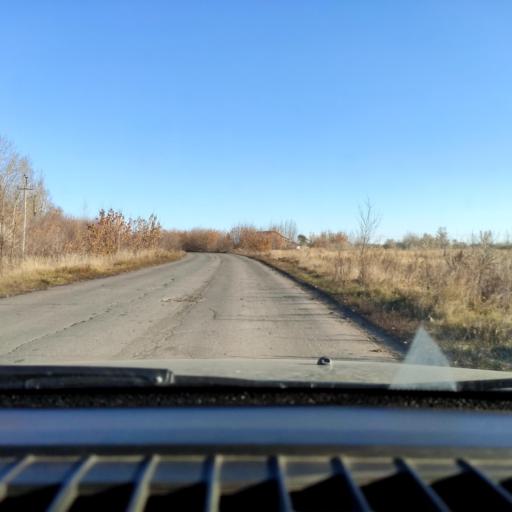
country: RU
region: Samara
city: Tol'yatti
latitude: 53.6391
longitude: 49.3129
